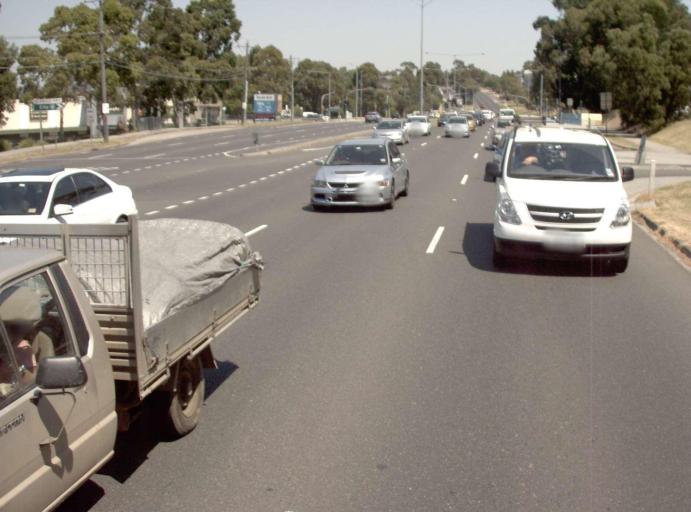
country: AU
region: Victoria
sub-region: Whitehorse
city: Vermont South
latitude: -37.8531
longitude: 145.1694
